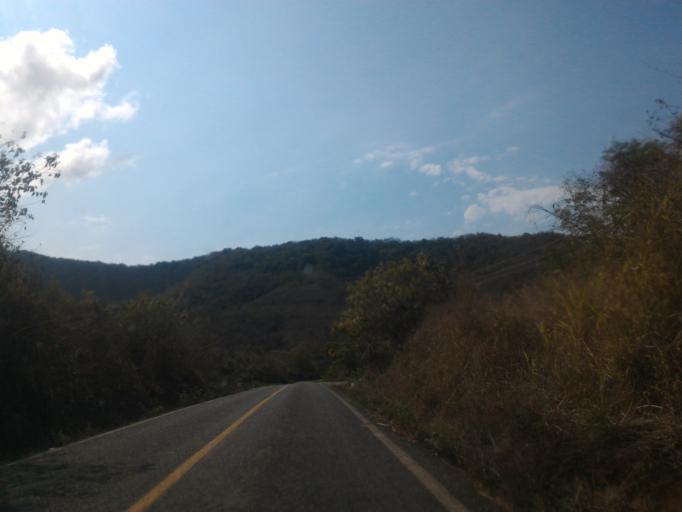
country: MX
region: Michoacan
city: Coahuayana Viejo
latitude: 18.4973
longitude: -103.5706
